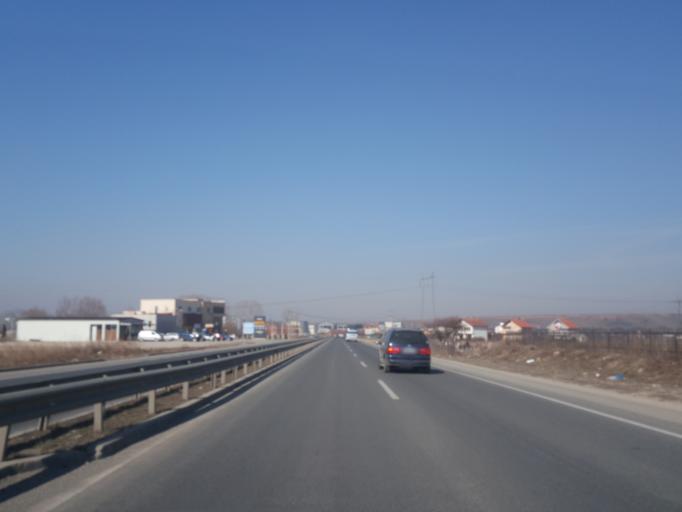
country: XK
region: Pristina
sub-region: Komuna e Obiliqit
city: Obiliq
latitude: 42.7302
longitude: 21.0750
